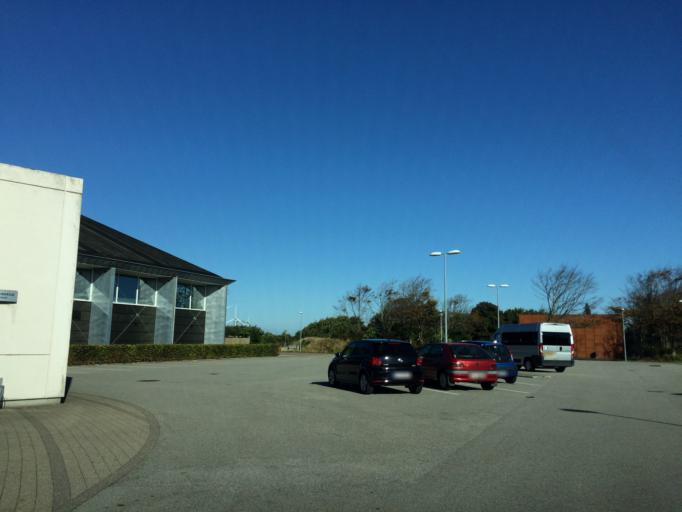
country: DK
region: Central Jutland
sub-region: Holstebro Kommune
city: Ulfborg
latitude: 56.2779
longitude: 8.3201
